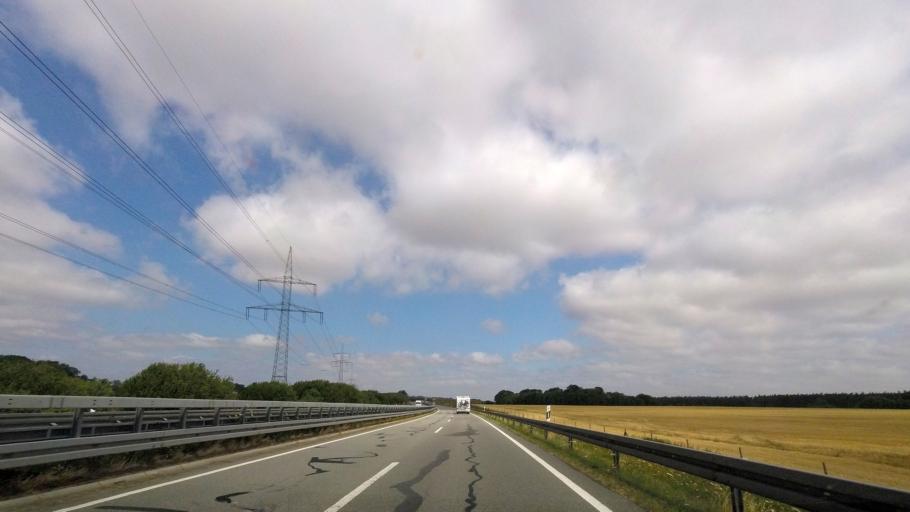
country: DE
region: Mecklenburg-Vorpommern
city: Brandshagen
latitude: 54.2010
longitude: 13.1574
